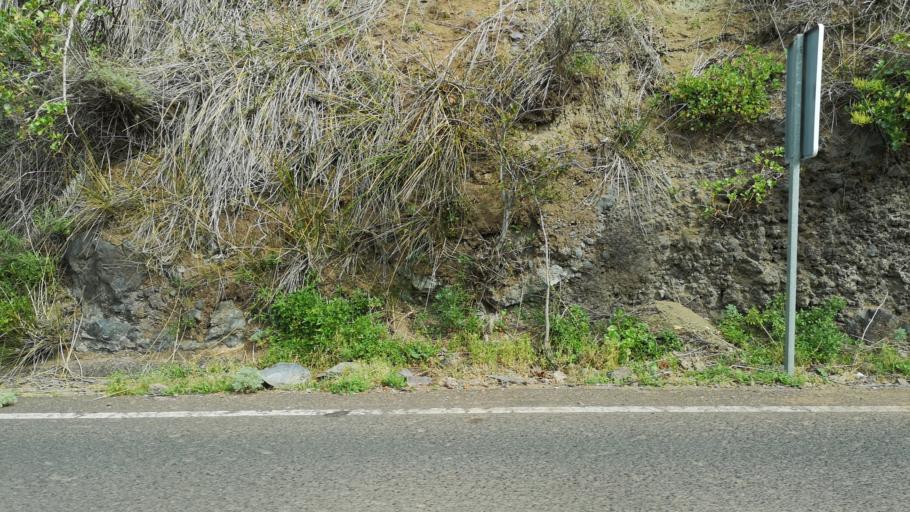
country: ES
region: Canary Islands
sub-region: Provincia de Santa Cruz de Tenerife
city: Vallehermosa
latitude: 28.1265
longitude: -17.3217
